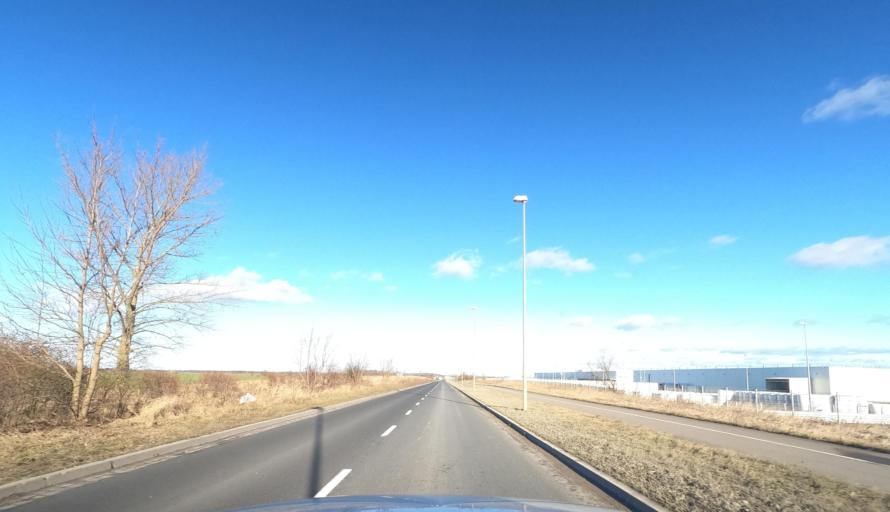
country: PL
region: West Pomeranian Voivodeship
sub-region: Powiat pyrzycki
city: Warnice
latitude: 53.3011
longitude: 14.9691
